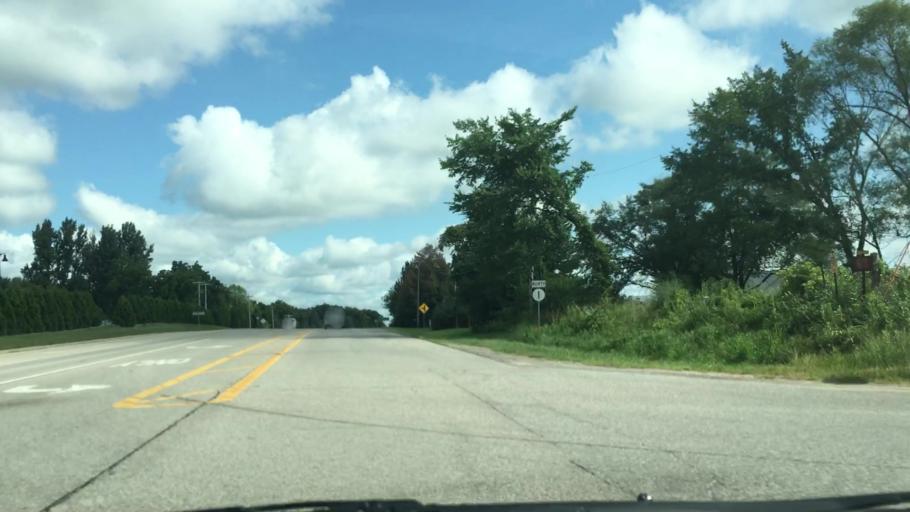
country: US
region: Iowa
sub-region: Johnson County
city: Solon
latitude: 41.7386
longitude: -91.4739
